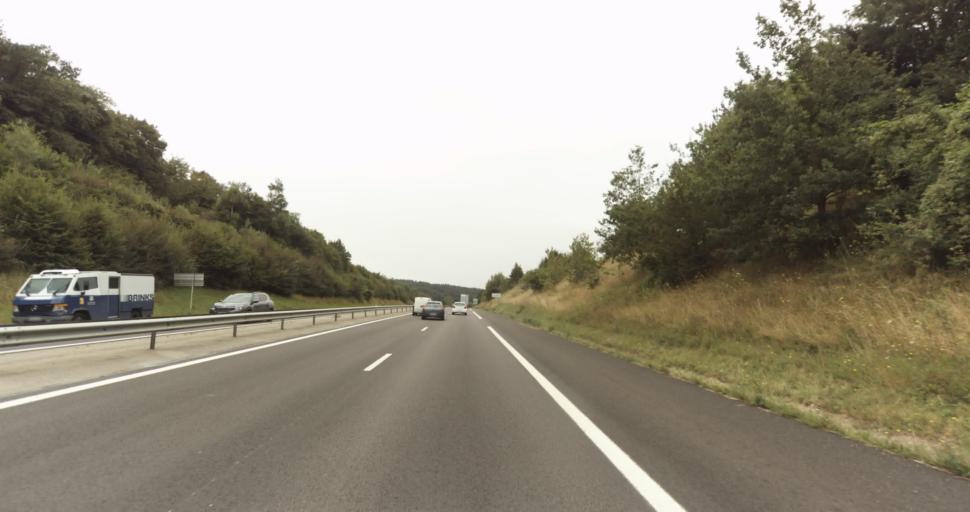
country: FR
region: Haute-Normandie
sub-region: Departement de l'Eure
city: Acquigny
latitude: 49.1653
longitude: 1.1757
